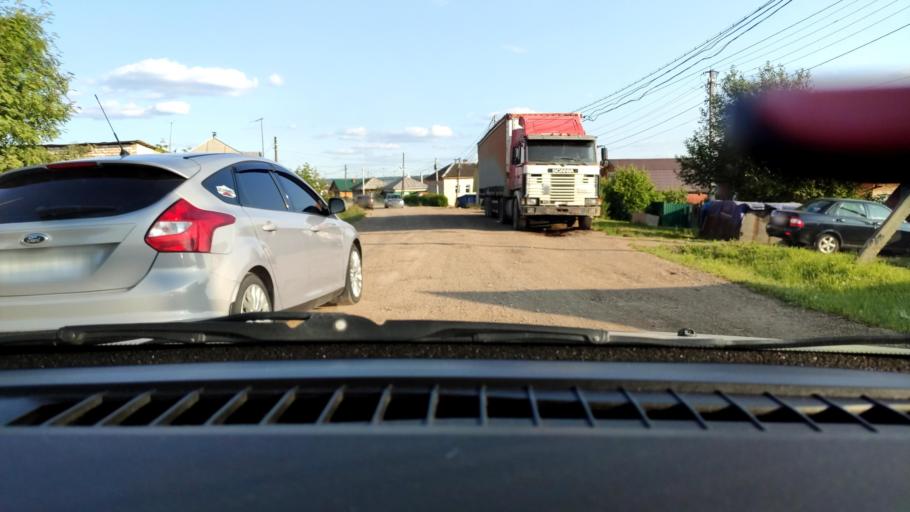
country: RU
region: Perm
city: Zvezdnyy
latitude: 57.7947
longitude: 56.3172
